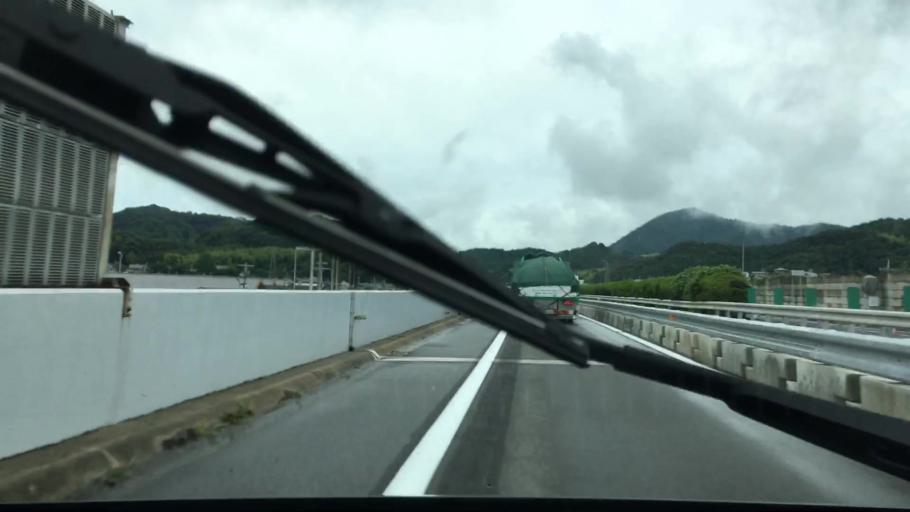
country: JP
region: Hyogo
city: Himeji
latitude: 34.9517
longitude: 134.7490
